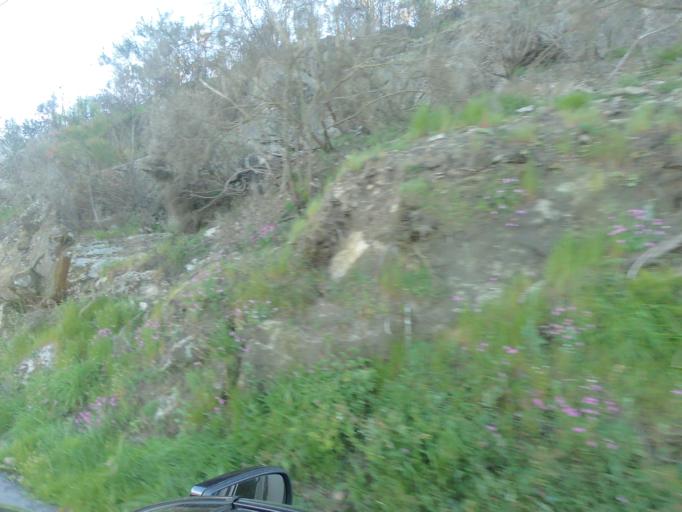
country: PT
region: Vila Real
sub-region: Vila Real
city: Vila Real
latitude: 41.3477
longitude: -7.7476
